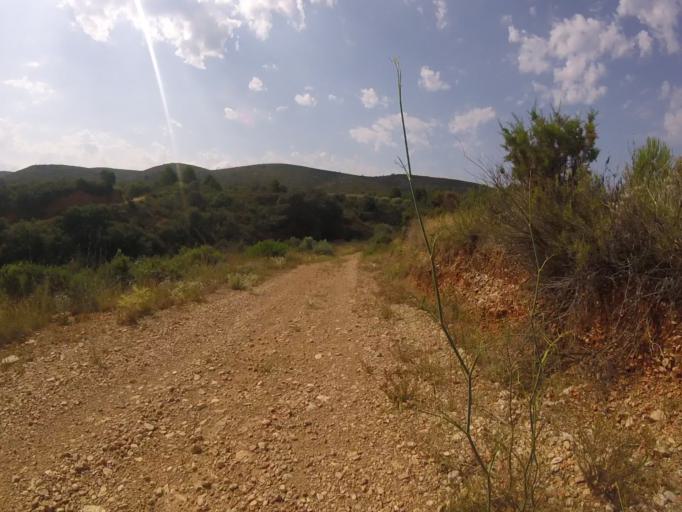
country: ES
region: Valencia
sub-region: Provincia de Castello
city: Alcala de Xivert
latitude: 40.3363
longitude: 0.1980
